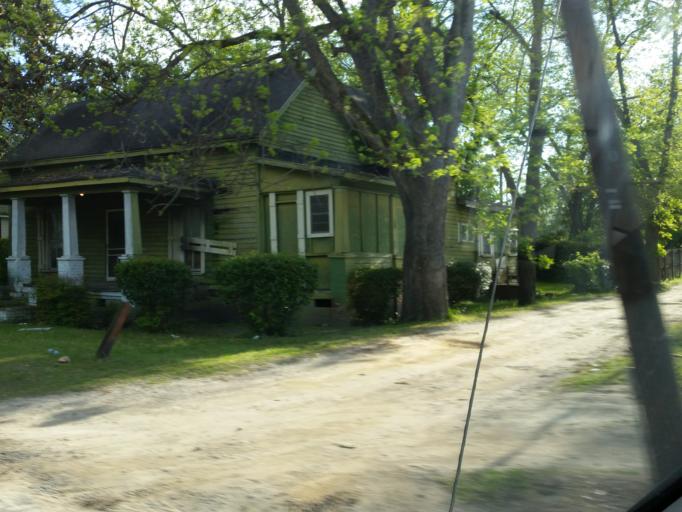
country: US
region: Georgia
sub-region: Crisp County
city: Cordele
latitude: 31.9653
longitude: -83.7881
